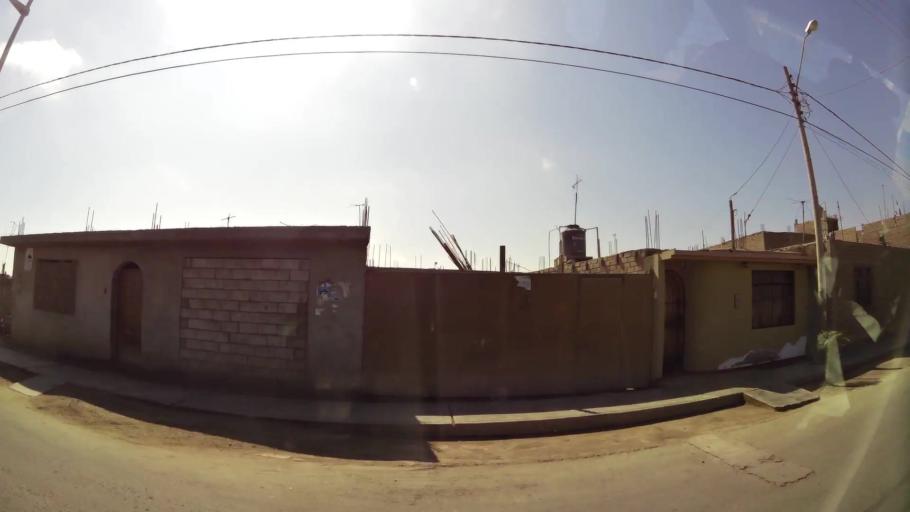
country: PE
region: Ica
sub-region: Provincia de Chincha
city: Sunampe
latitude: -13.4209
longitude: -76.1673
